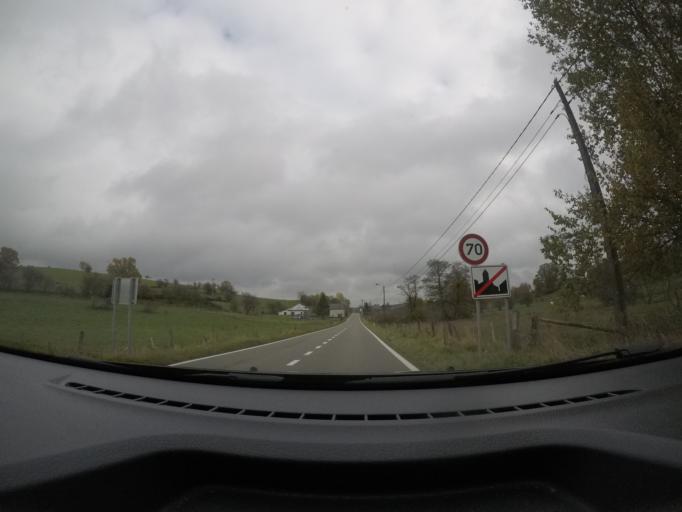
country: BE
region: Wallonia
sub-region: Province du Luxembourg
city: Bertogne
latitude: 50.0880
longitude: 5.7119
